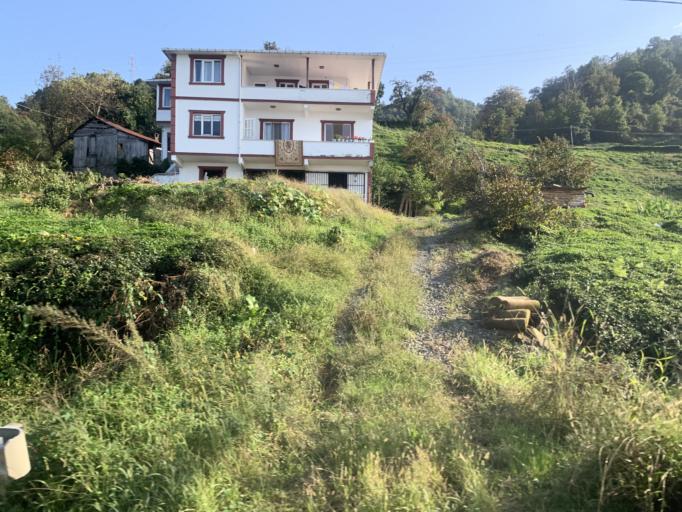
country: TR
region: Trabzon
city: Of
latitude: 40.9344
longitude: 40.2444
